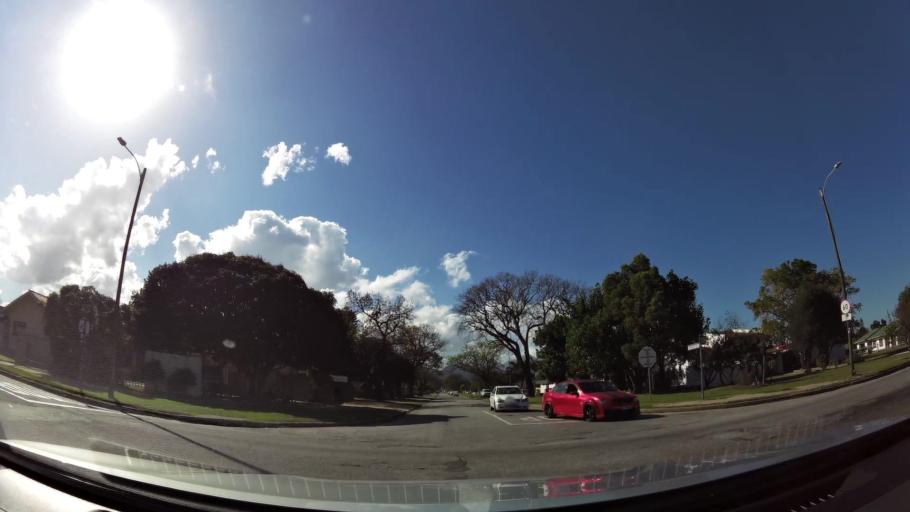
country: ZA
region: Western Cape
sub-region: Eden District Municipality
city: George
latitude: -33.9735
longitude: 22.4496
